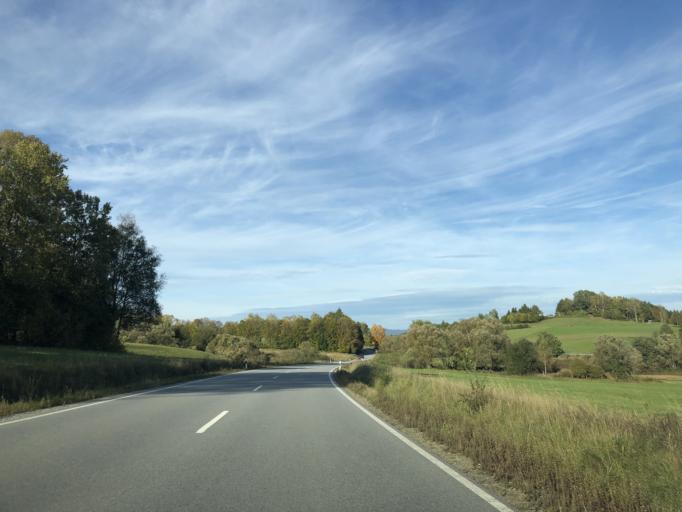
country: DE
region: Bavaria
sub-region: Lower Bavaria
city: Gotteszell
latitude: 48.9718
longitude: 12.9777
